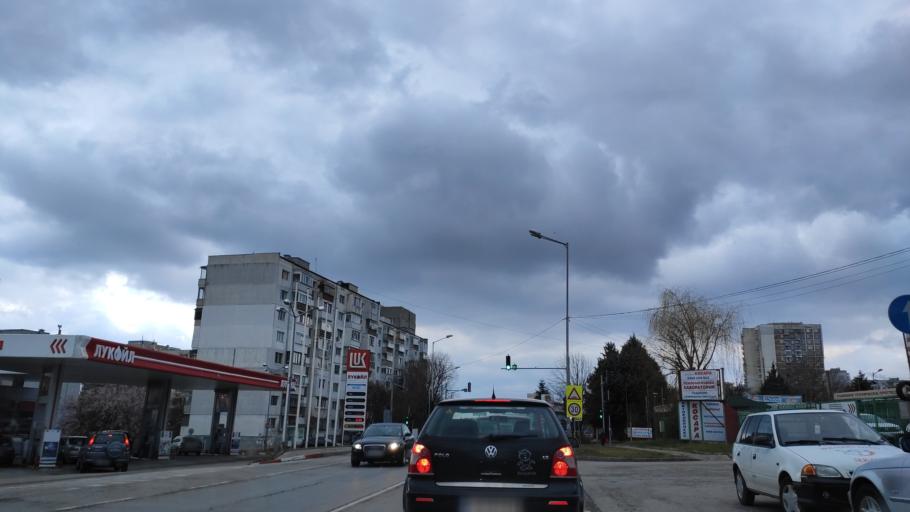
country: BG
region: Varna
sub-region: Obshtina Varna
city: Varna
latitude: 43.2345
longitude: 27.8775
